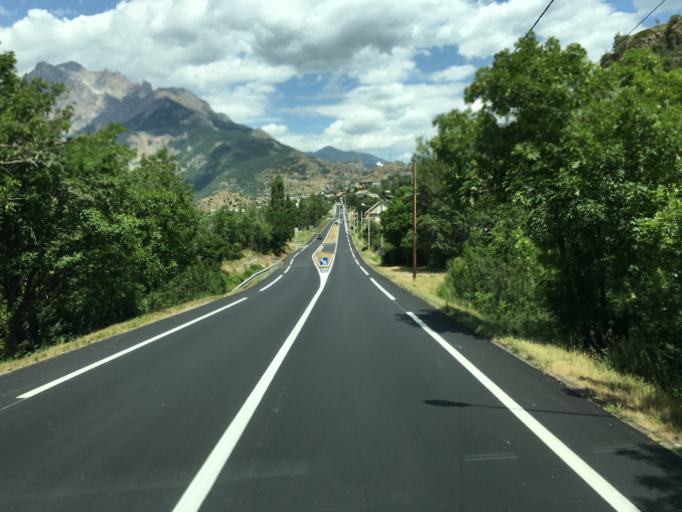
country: FR
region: Provence-Alpes-Cote d'Azur
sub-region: Departement des Hautes-Alpes
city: Saint-Martin-de-Queyrieres
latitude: 44.7867
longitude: 6.5611
